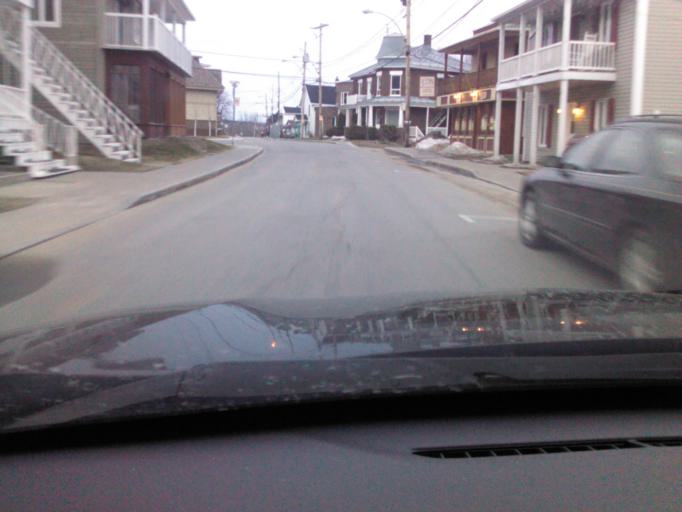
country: CA
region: Quebec
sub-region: Capitale-Nationale
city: Donnacona
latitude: 46.6729
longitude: -71.7368
